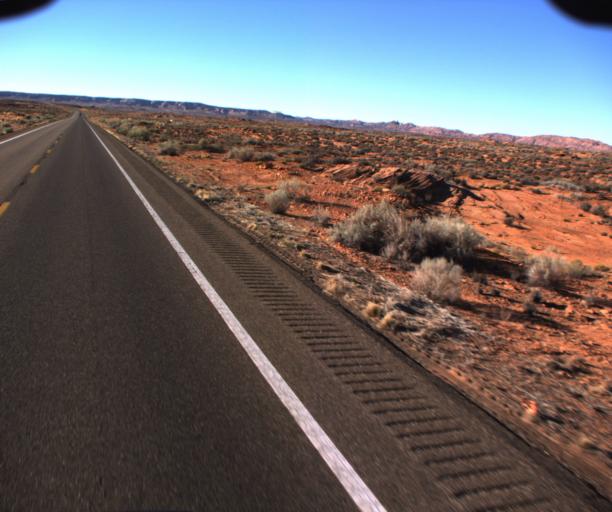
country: US
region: Arizona
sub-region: Coconino County
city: LeChee
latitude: 36.8597
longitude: -111.5056
